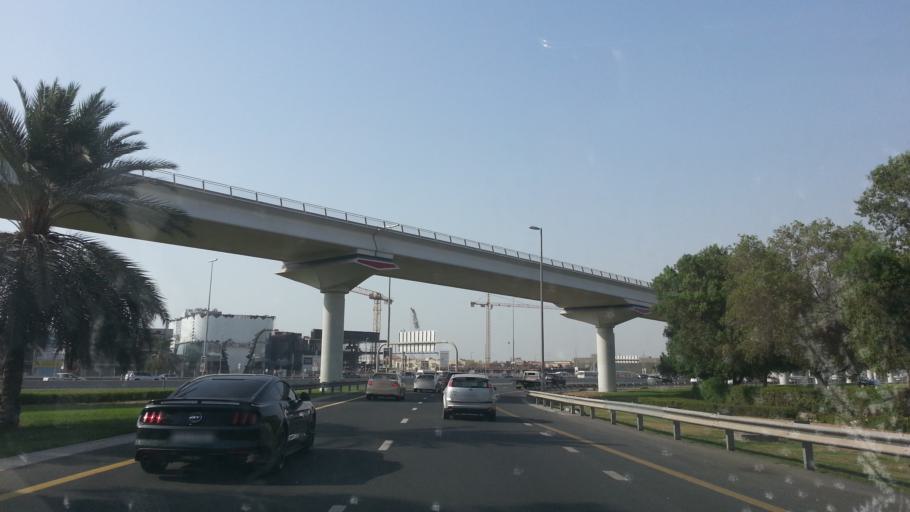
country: AE
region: Dubai
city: Dubai
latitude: 25.1229
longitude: 55.2040
